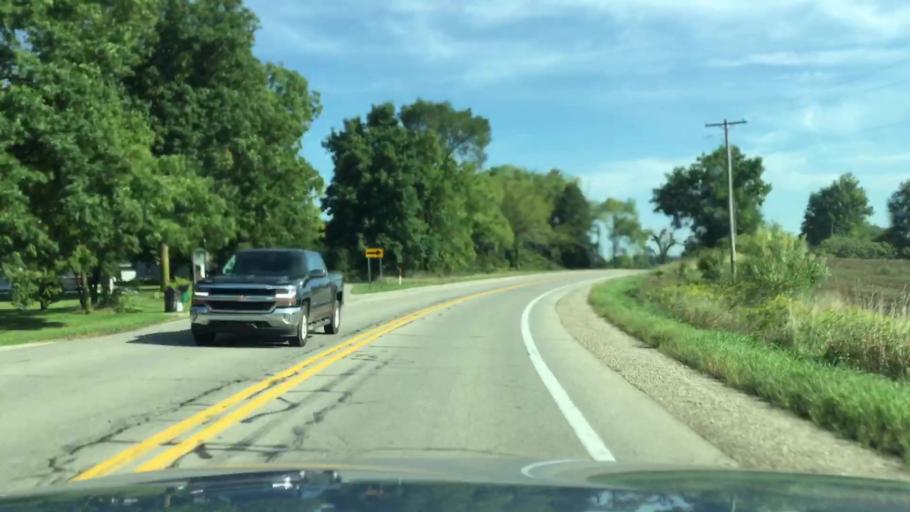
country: US
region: Michigan
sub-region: Lenawee County
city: Manitou Beach-Devils Lake
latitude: 41.9625
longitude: -84.3671
